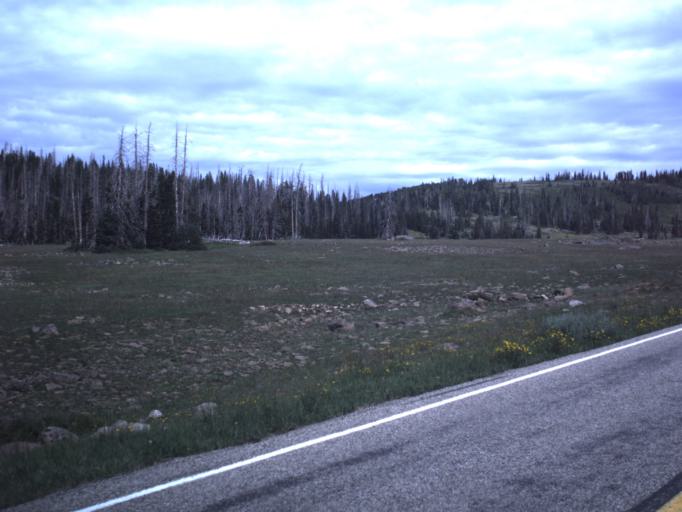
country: US
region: Utah
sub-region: Iron County
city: Cedar City
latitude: 37.5904
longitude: -112.8490
